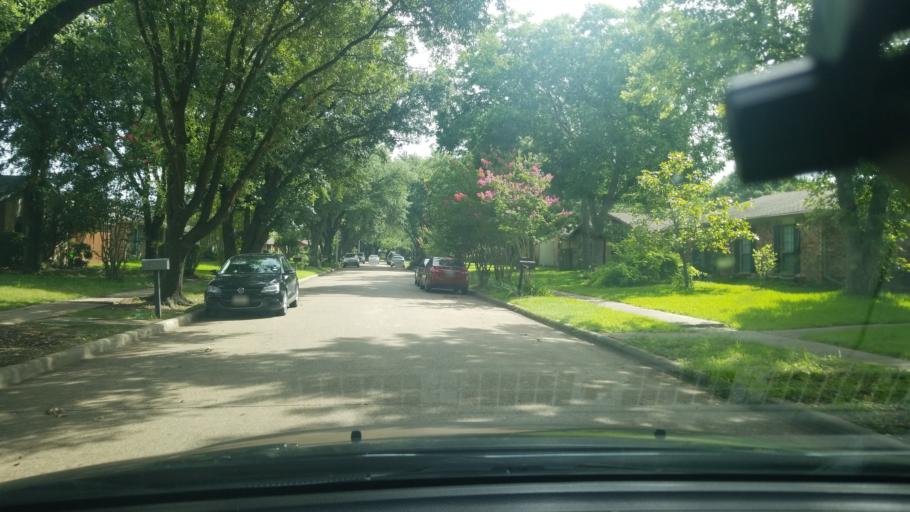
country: US
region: Texas
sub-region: Dallas County
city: Highland Park
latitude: 32.8026
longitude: -96.6957
